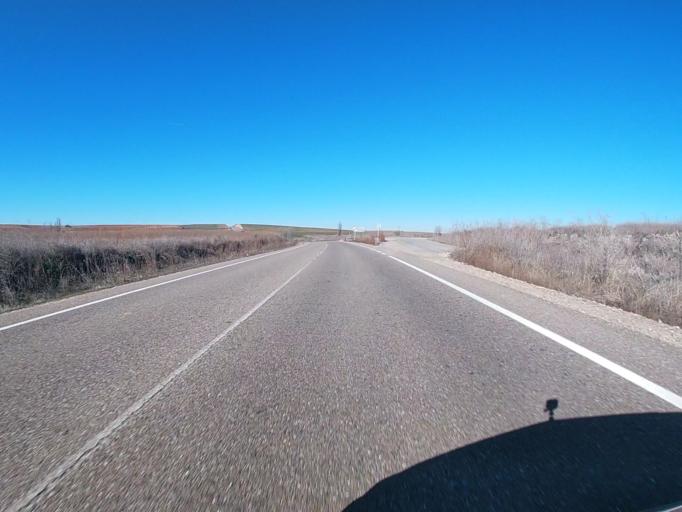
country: ES
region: Castille and Leon
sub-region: Provincia de Salamanca
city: Almenara de Tormes
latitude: 41.0665
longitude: -5.8255
